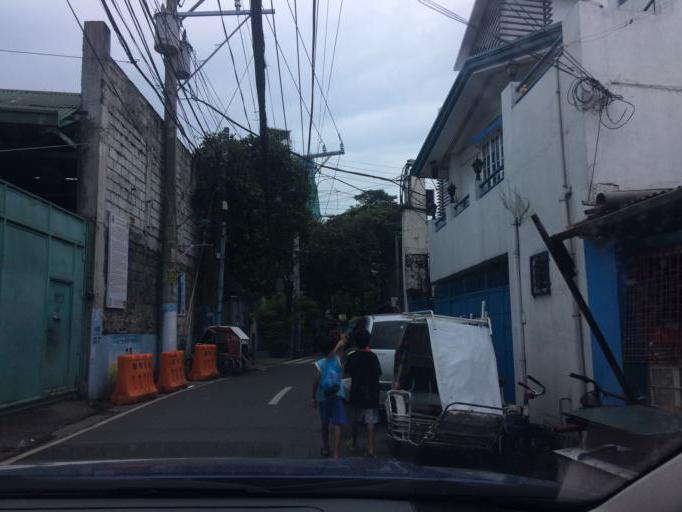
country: PH
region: Metro Manila
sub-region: Makati City
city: Makati City
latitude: 14.5359
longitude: 121.0017
